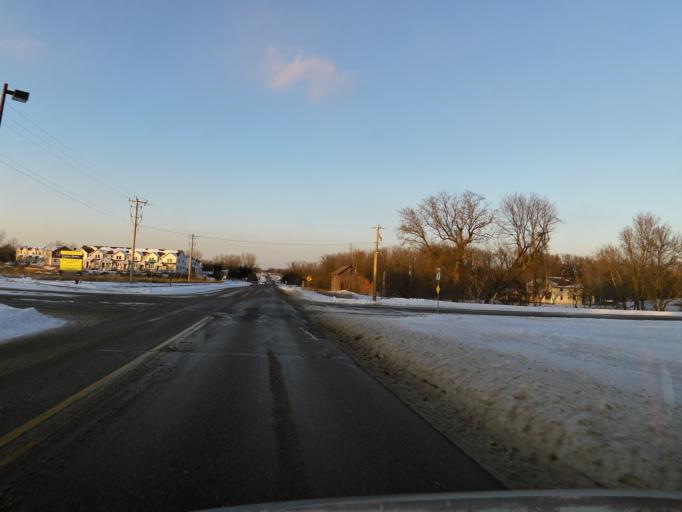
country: US
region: Minnesota
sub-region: Washington County
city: Lake Elmo
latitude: 44.9375
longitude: -92.8833
